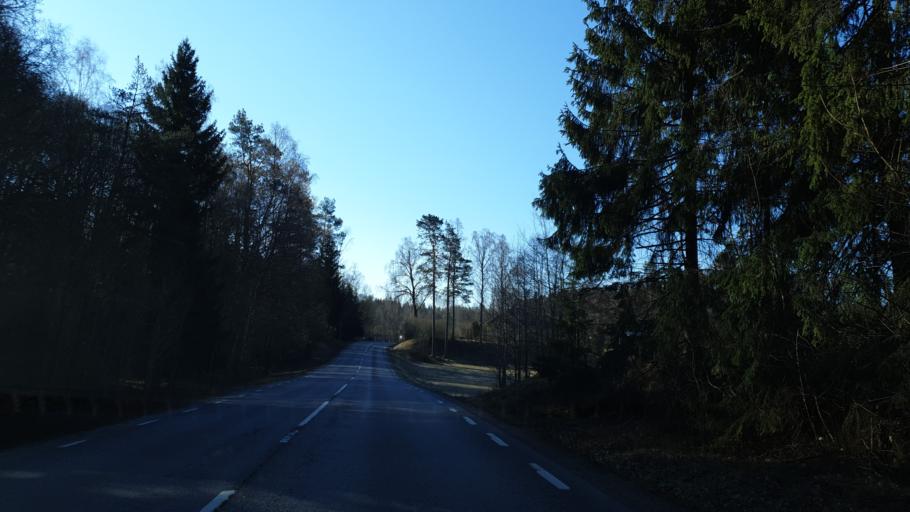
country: SE
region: Vaestra Goetaland
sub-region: Boras Kommun
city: Dalsjofors
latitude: 57.7499
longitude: 13.1084
